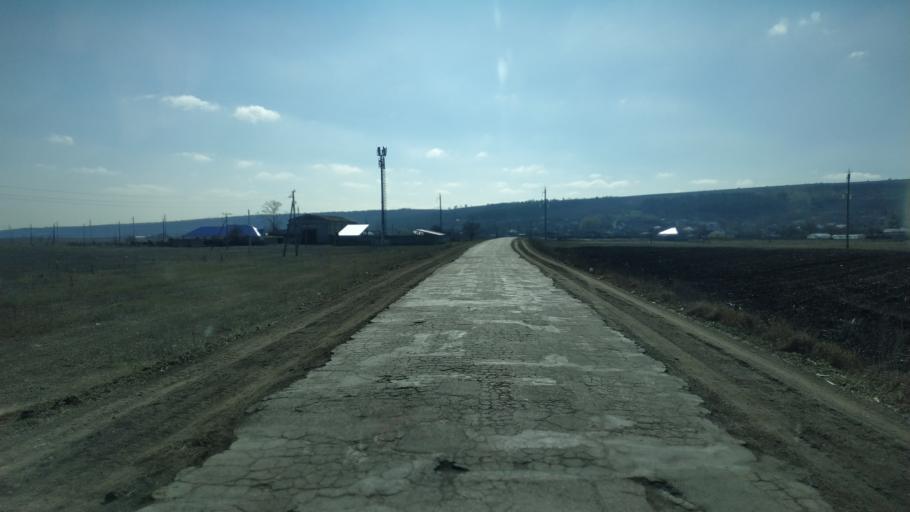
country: MD
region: Hincesti
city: Hincesti
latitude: 46.7539
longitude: 28.6526
